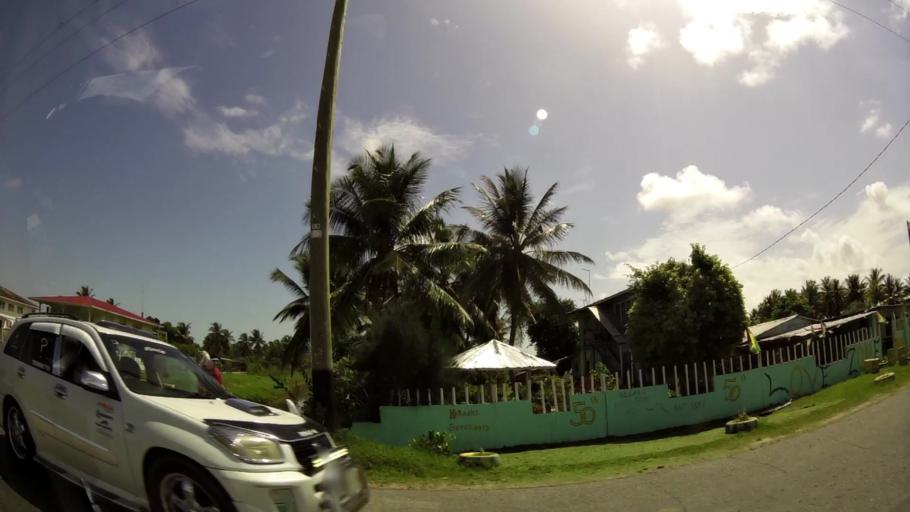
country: GY
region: Demerara-Mahaica
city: Mahaica Village
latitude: 6.7655
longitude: -57.9972
